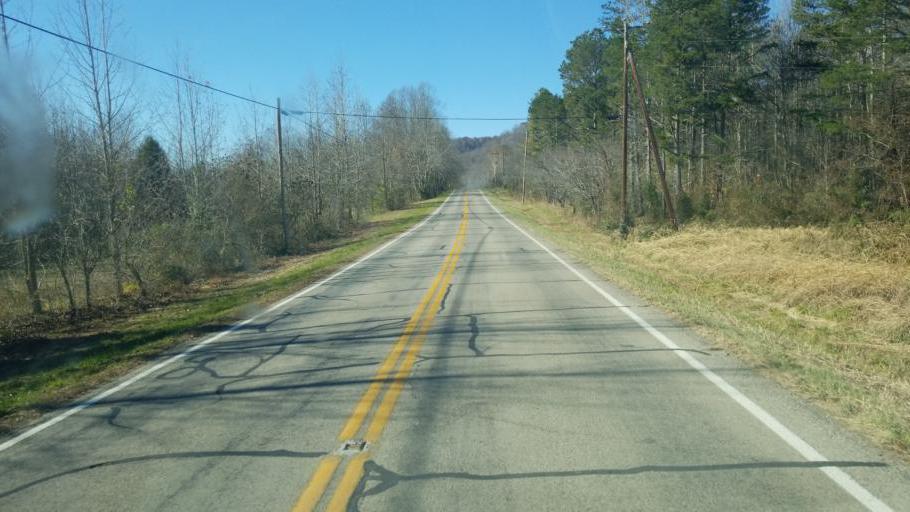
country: US
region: Kentucky
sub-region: Lewis County
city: Vanceburg
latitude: 38.6377
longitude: -83.2255
